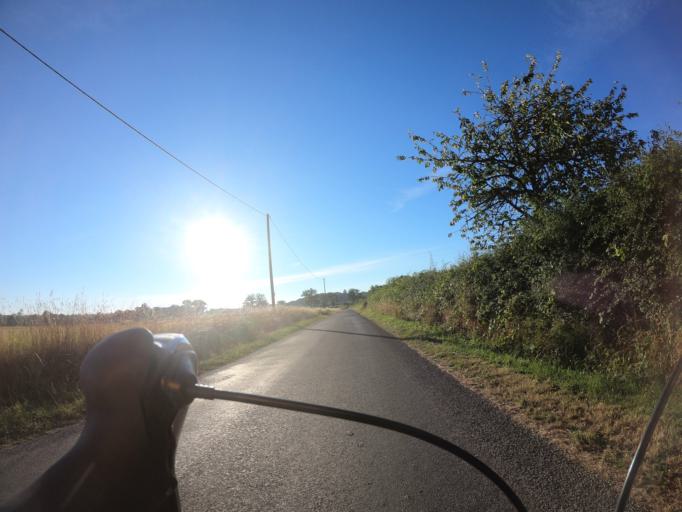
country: FR
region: Lower Normandy
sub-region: Departement de l'Orne
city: Magny-le-Desert
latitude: 48.5388
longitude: -0.2961
